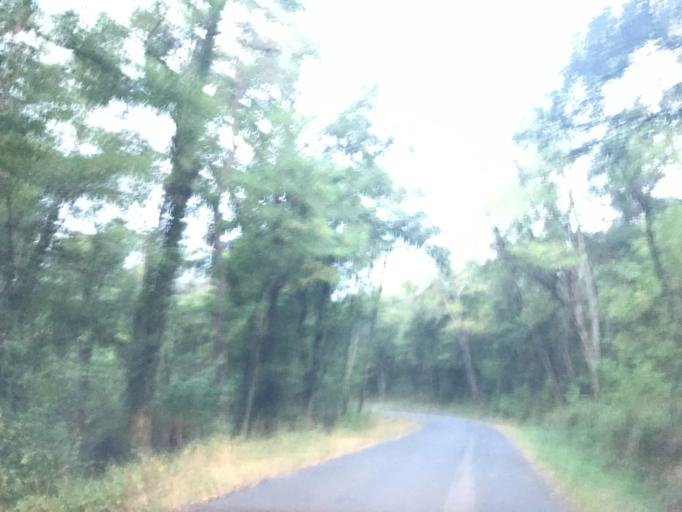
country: FR
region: Auvergne
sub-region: Departement du Puy-de-Dome
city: Escoutoux
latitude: 45.7913
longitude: 3.5699
